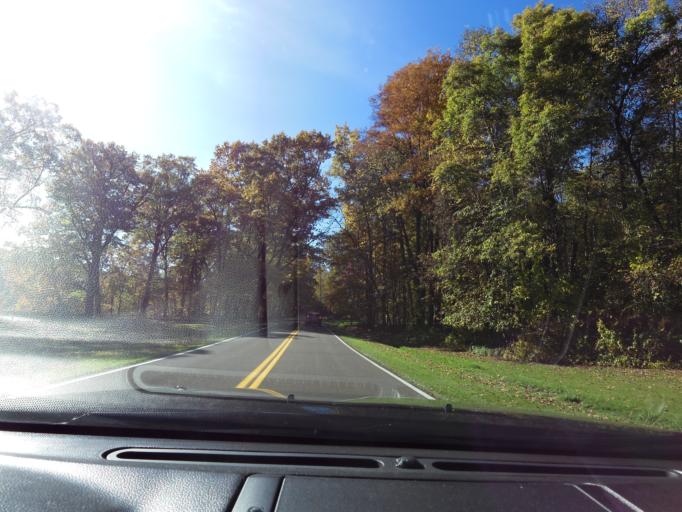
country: US
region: New York
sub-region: Wyoming County
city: Castile
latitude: 42.6116
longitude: -78.0175
